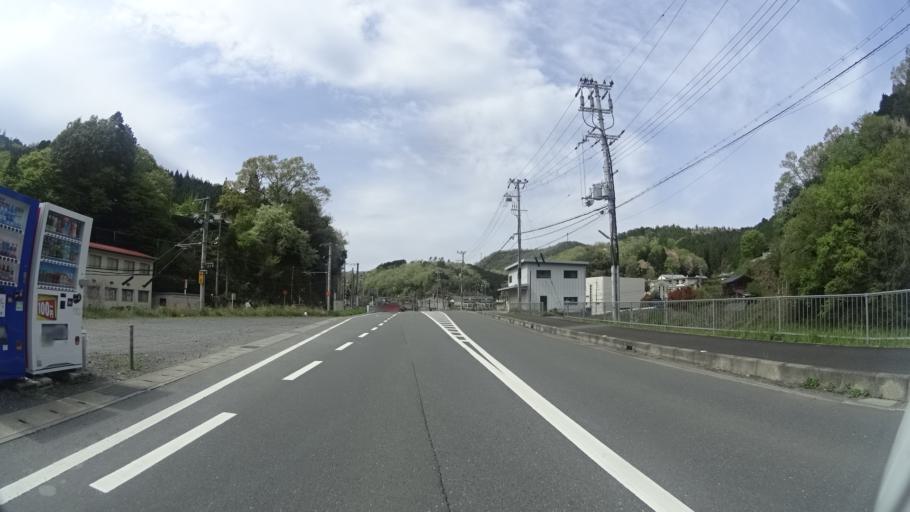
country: JP
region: Kyoto
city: Kameoka
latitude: 35.1576
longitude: 135.5065
